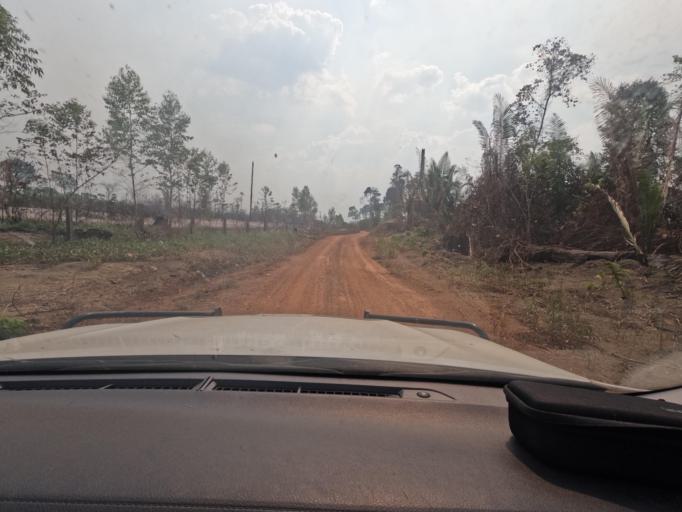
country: BR
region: Rondonia
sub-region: Porto Velho
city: Porto Velho
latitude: -8.7730
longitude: -63.2043
